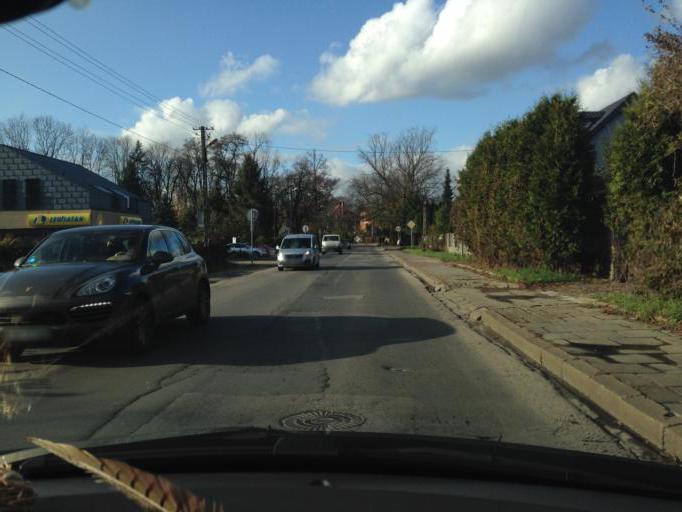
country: PL
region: Lesser Poland Voivodeship
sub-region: Powiat krakowski
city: Rzaska
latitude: 50.0638
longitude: 19.8837
